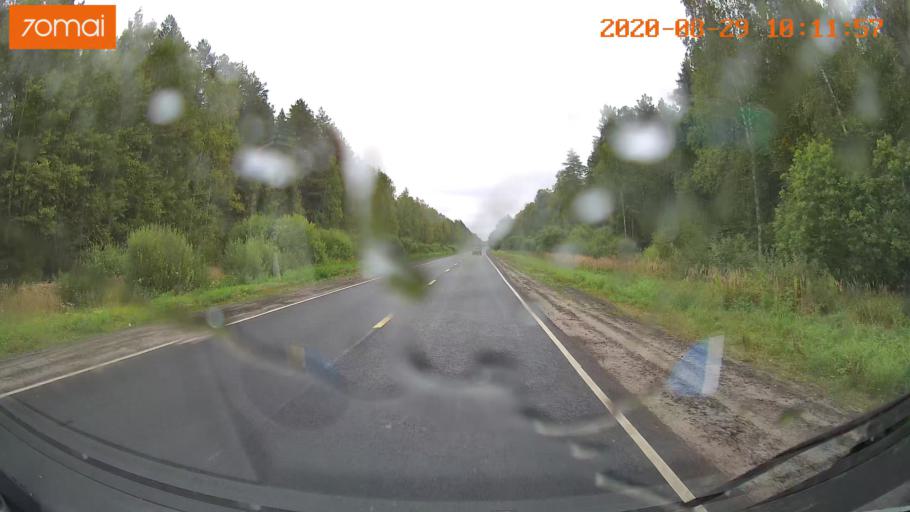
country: RU
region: Ivanovo
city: Kuznechikha
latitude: 57.3739
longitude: 42.6971
